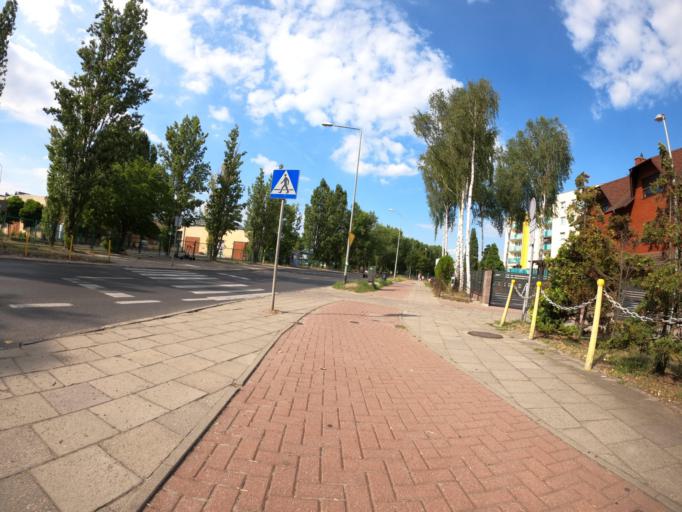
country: PL
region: West Pomeranian Voivodeship
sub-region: Szczecin
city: Szczecin
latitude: 53.3816
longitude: 14.6522
